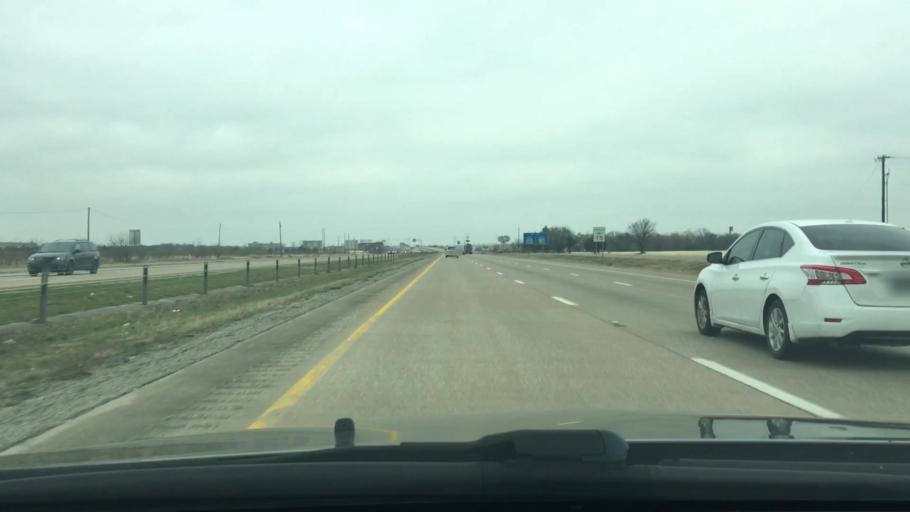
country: US
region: Texas
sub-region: Ellis County
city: Ennis
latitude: 32.3194
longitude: -96.6051
